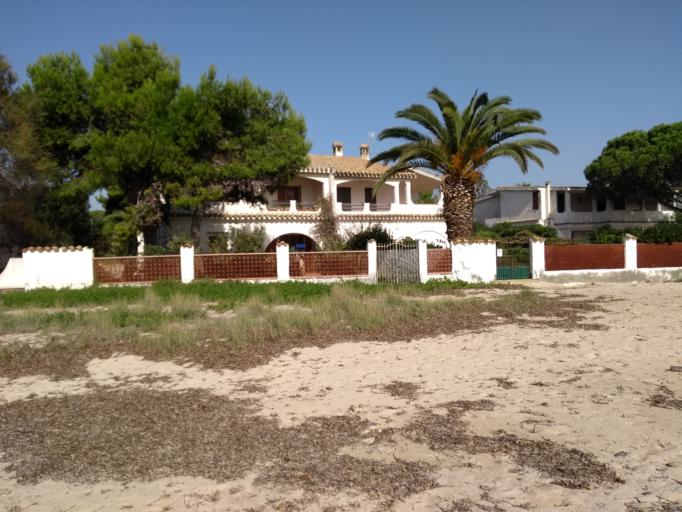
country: IT
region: Sardinia
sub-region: Provincia di Cagliari
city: Quartu Sant'Elena
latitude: 39.2142
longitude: 9.2833
